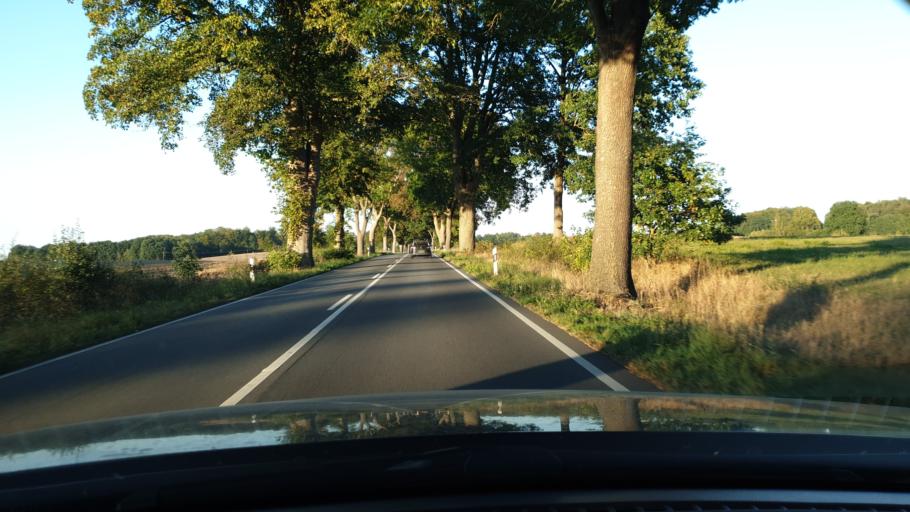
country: DE
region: Mecklenburg-Vorpommern
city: Lutzow
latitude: 53.5928
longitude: 11.1228
